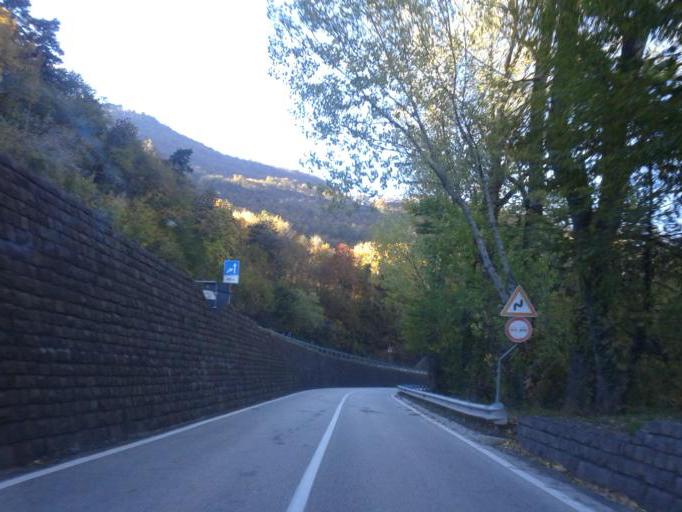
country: IT
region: Trentino-Alto Adige
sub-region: Provincia di Trento
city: Trento
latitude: 46.0745
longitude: 11.1032
